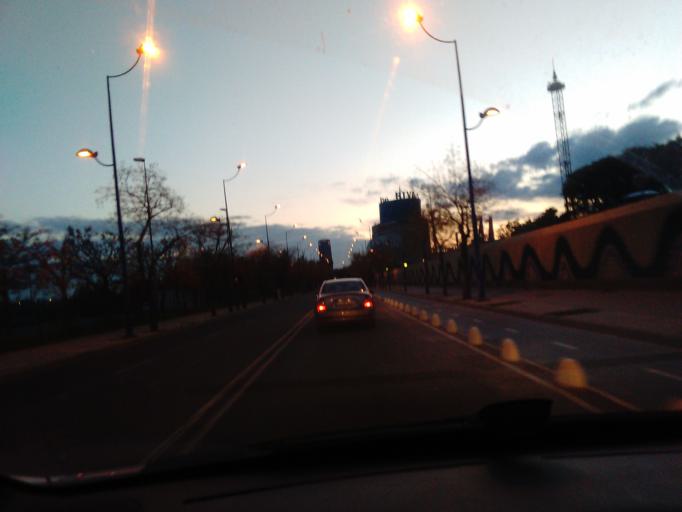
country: ES
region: Andalusia
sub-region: Provincia de Sevilla
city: Sevilla
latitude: 37.4080
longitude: -5.9968
